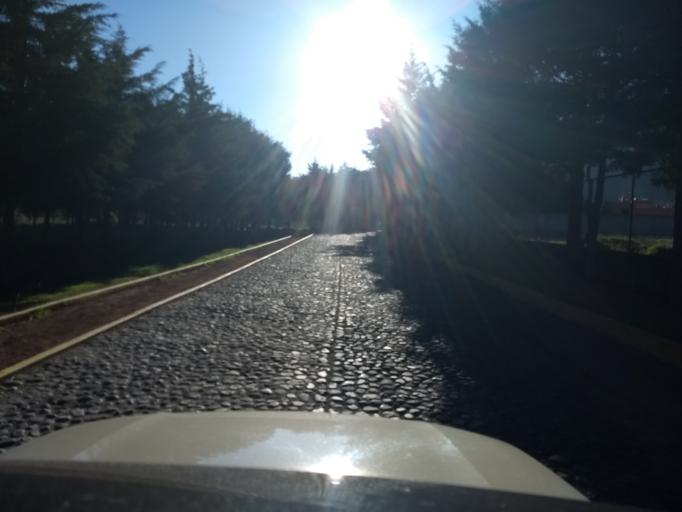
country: MX
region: Mexico
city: San Marcos Yachihuacaltepec
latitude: 19.3072
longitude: -99.6907
